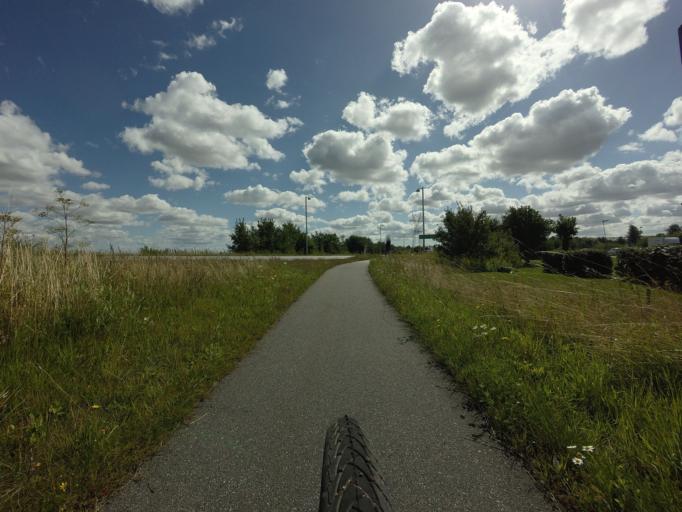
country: DK
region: Central Jutland
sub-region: Horsens Kommune
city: Horsens
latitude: 55.8864
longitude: 9.7880
